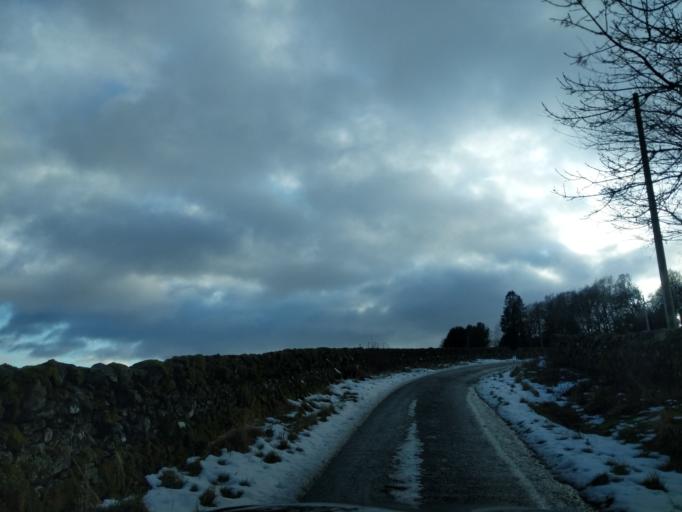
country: GB
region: Scotland
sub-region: Dumfries and Galloway
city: Moffat
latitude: 55.3224
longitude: -3.4777
